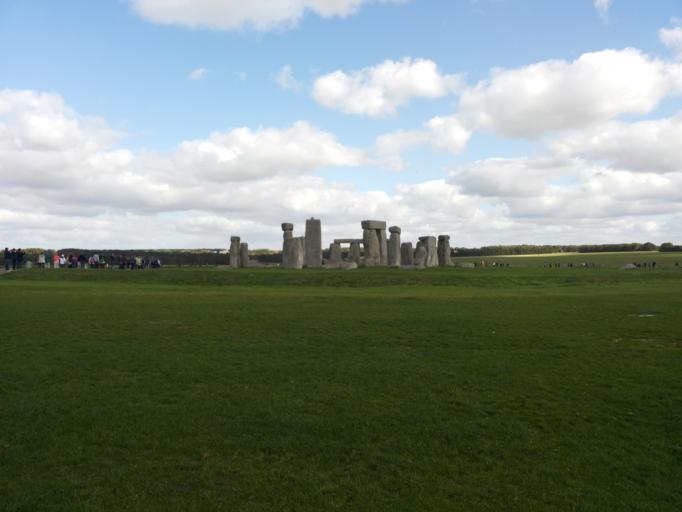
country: GB
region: England
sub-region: Wiltshire
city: Durnford
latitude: 51.1782
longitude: -1.8268
